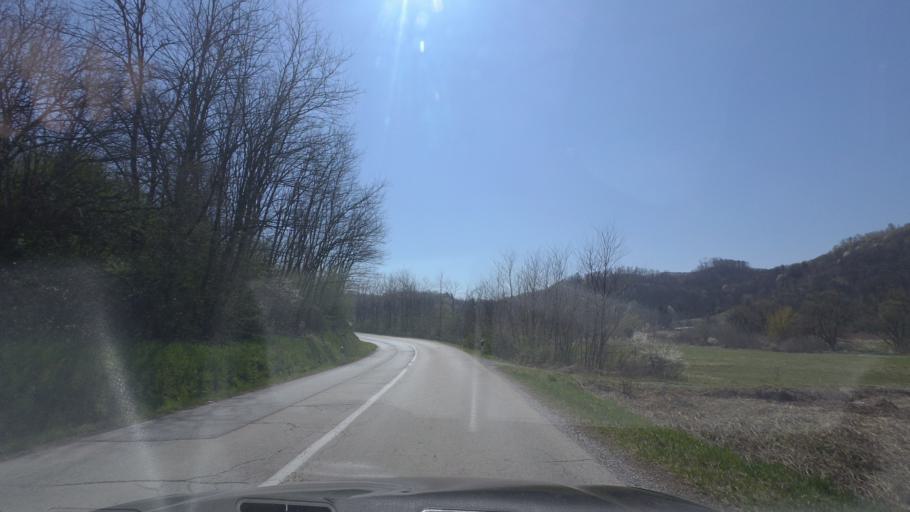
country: HR
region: Karlovacka
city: Vojnic
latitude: 45.3508
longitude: 15.6765
